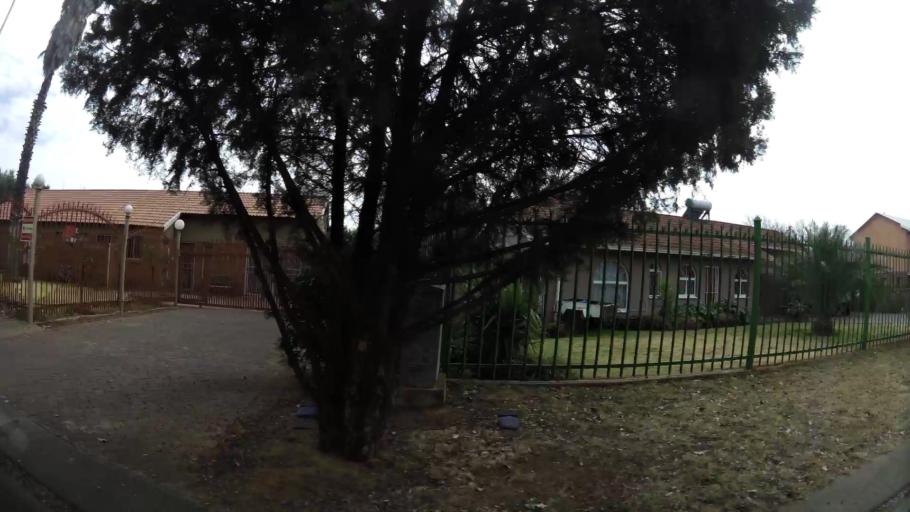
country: ZA
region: Orange Free State
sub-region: Mangaung Metropolitan Municipality
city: Bloemfontein
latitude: -29.1270
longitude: 26.1826
